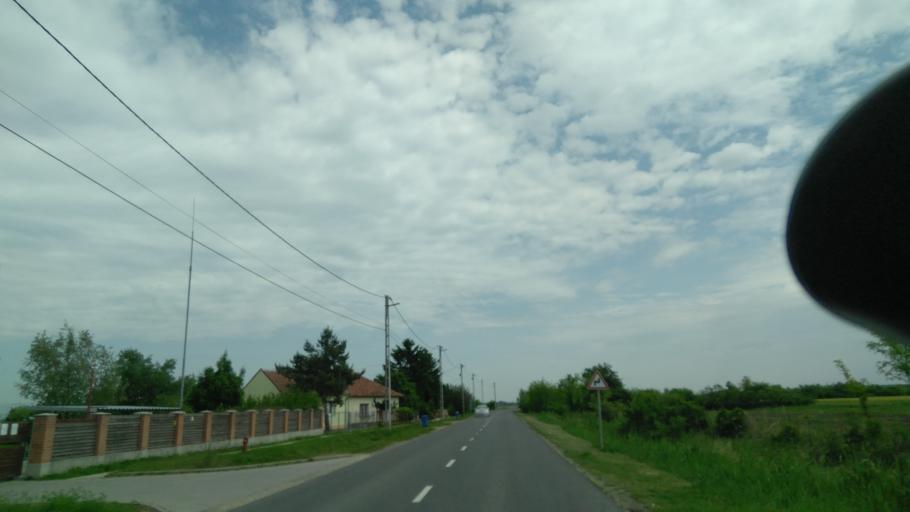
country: HU
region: Hajdu-Bihar
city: Komadi
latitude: 47.0147
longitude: 21.5114
